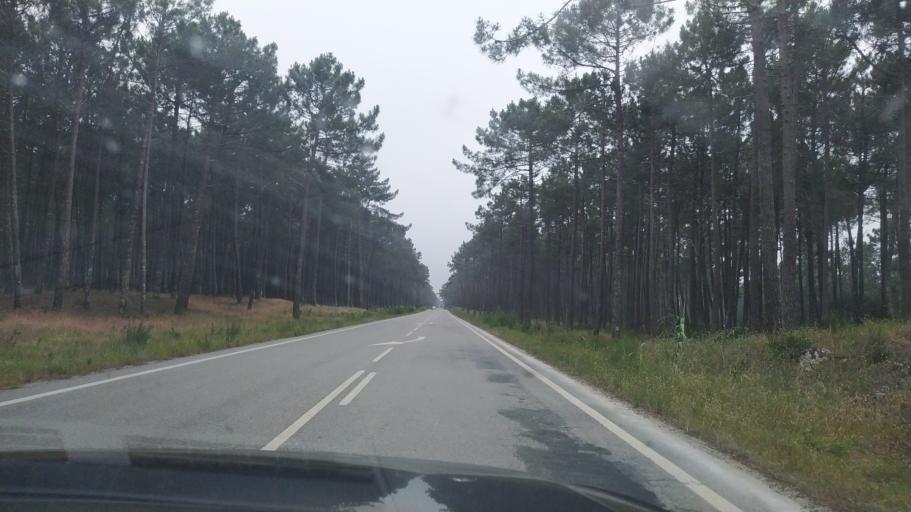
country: PT
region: Aveiro
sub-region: Ilhavo
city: Gafanha da Encarnacao
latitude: 40.5951
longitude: -8.7249
